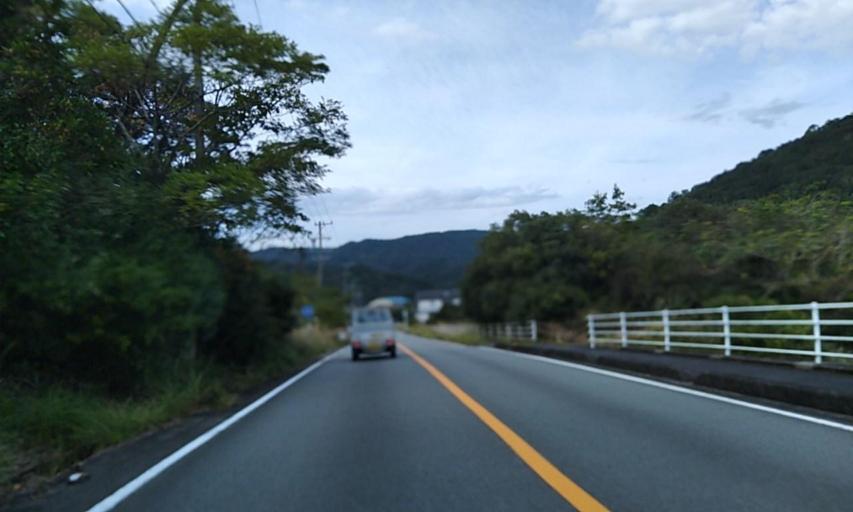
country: JP
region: Mie
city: Ise
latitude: 34.3027
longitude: 136.6371
